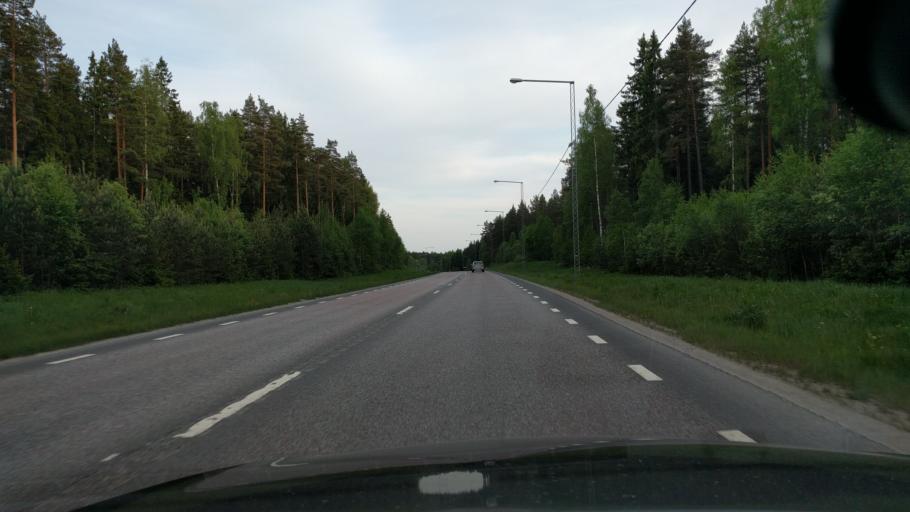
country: SE
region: Stockholm
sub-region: Vallentuna Kommun
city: Vallentuna
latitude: 59.5023
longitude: 18.0996
